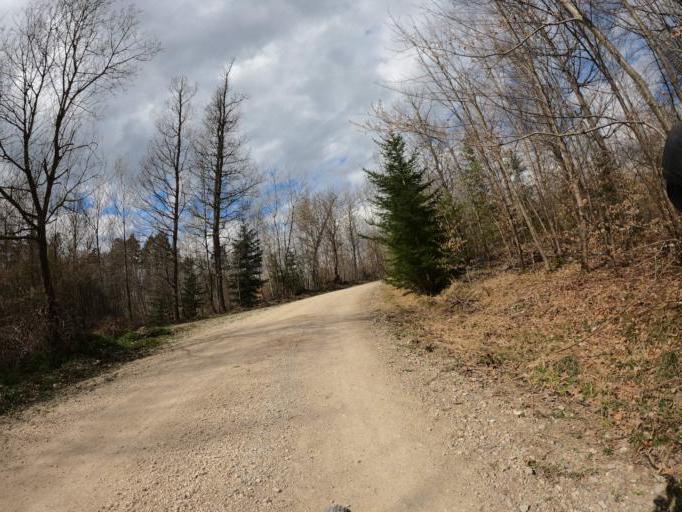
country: DE
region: Baden-Wuerttemberg
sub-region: Tuebingen Region
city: Gomaringen
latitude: 48.4564
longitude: 9.1276
